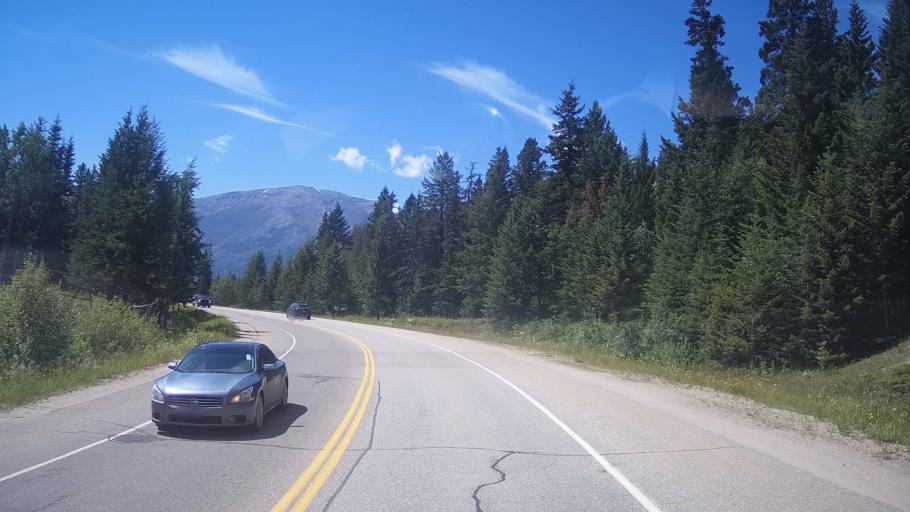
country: CA
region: Alberta
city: Jasper Park Lodge
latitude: 52.8938
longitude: -118.0750
